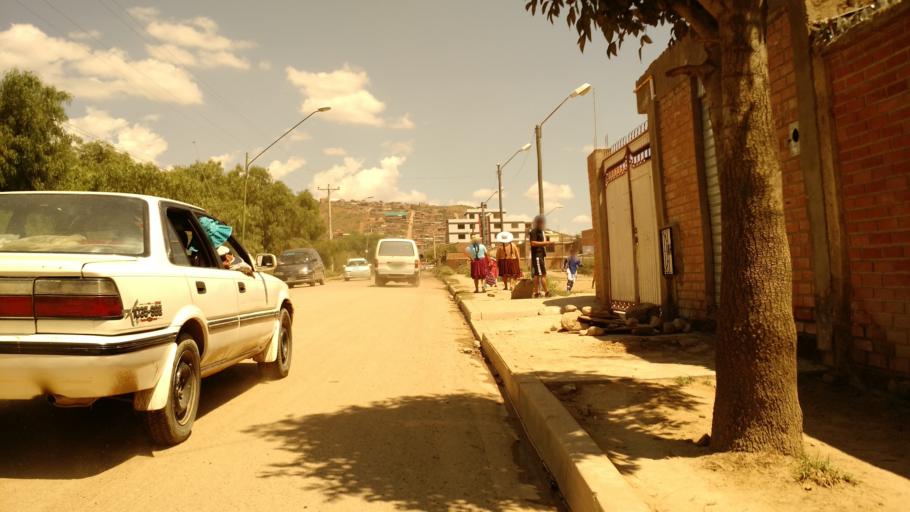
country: BO
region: Cochabamba
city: Cochabamba
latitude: -17.4548
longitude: -66.1564
